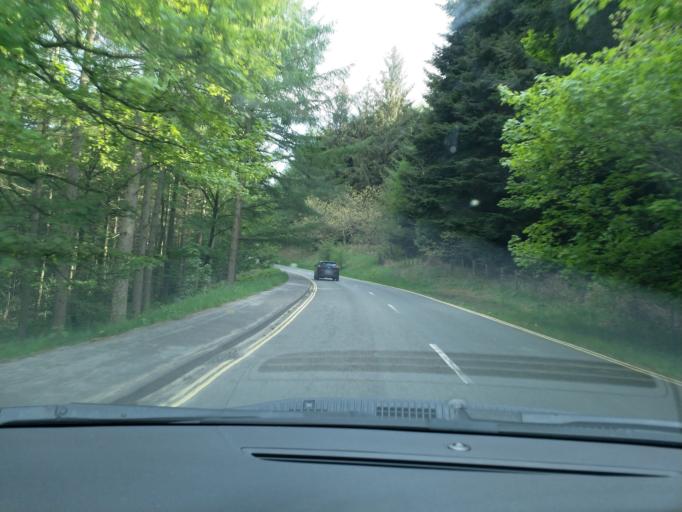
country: GB
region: England
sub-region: Derbyshire
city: Hope Valley
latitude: 53.3845
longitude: -1.7203
